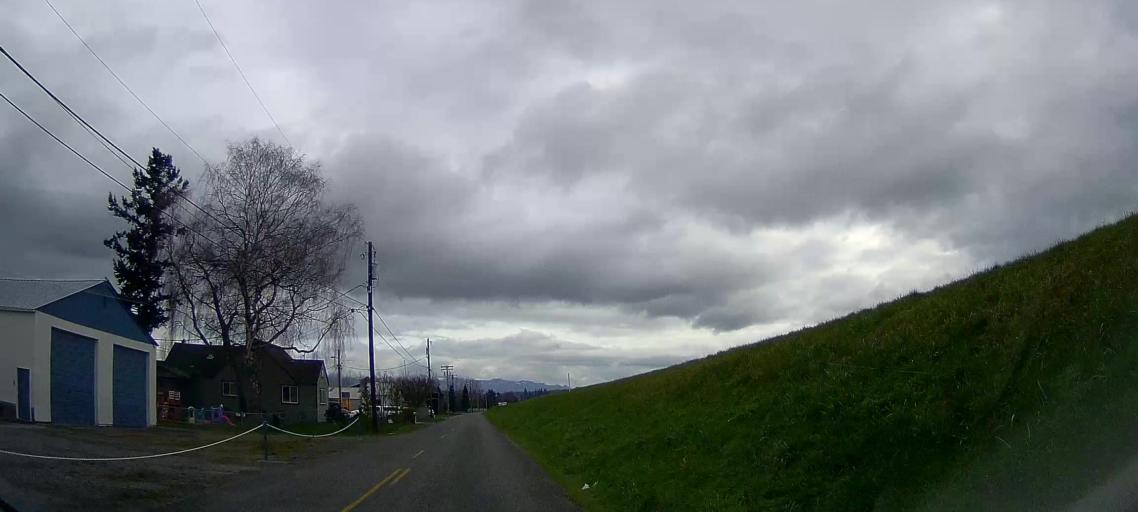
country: US
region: Washington
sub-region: Skagit County
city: Mount Vernon
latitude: 48.4335
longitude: -122.3645
